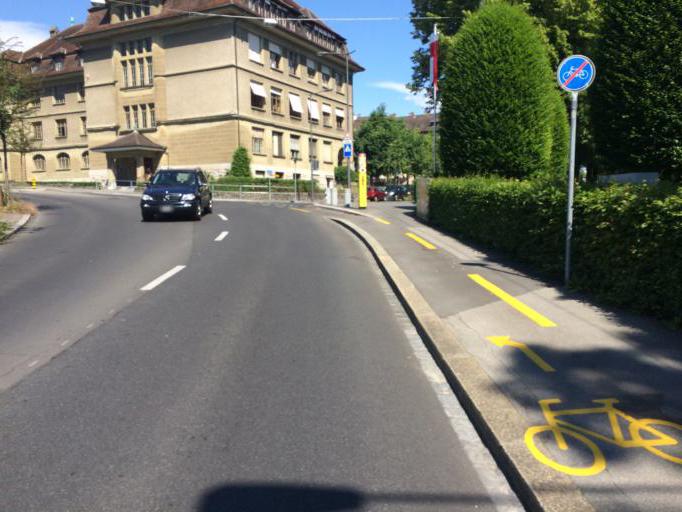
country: CH
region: Vaud
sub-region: Lausanne District
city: Lausanne
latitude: 46.5159
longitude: 6.6226
